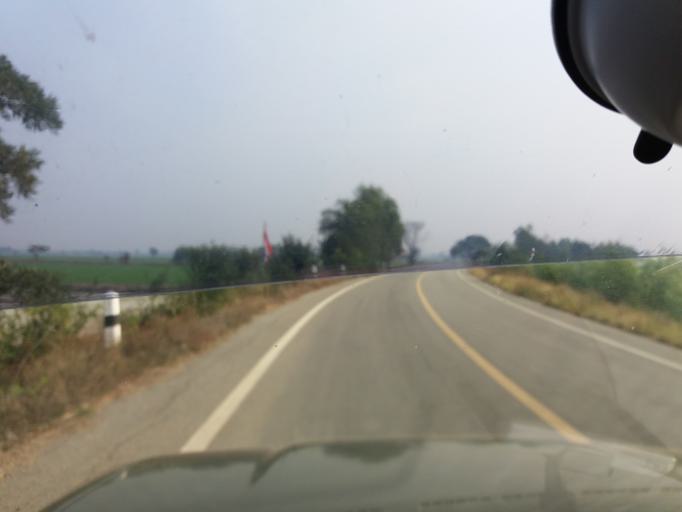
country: TH
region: Suphan Buri
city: Doem Bang Nang Buat
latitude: 14.8548
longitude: 100.1477
